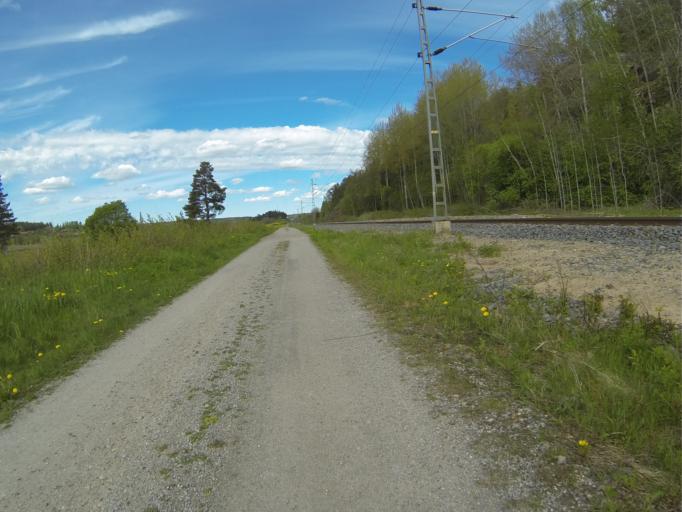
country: FI
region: Varsinais-Suomi
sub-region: Salo
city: Salo
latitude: 60.3611
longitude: 23.1179
